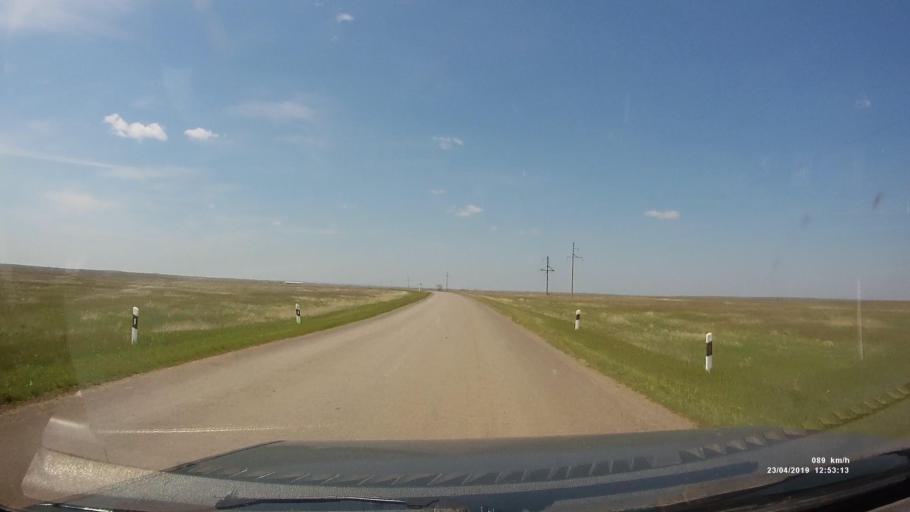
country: RU
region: Kalmykiya
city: Yashalta
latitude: 46.5717
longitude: 42.5996
